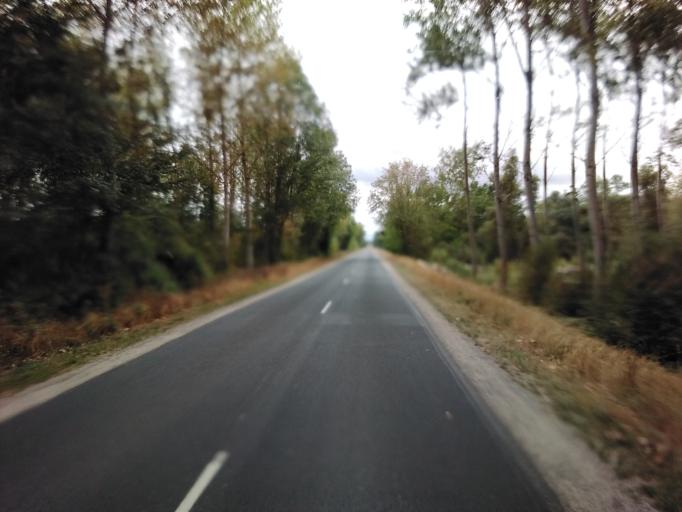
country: FR
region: Champagne-Ardenne
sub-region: Departement de la Marne
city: Frignicourt
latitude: 48.6864
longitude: 4.5822
